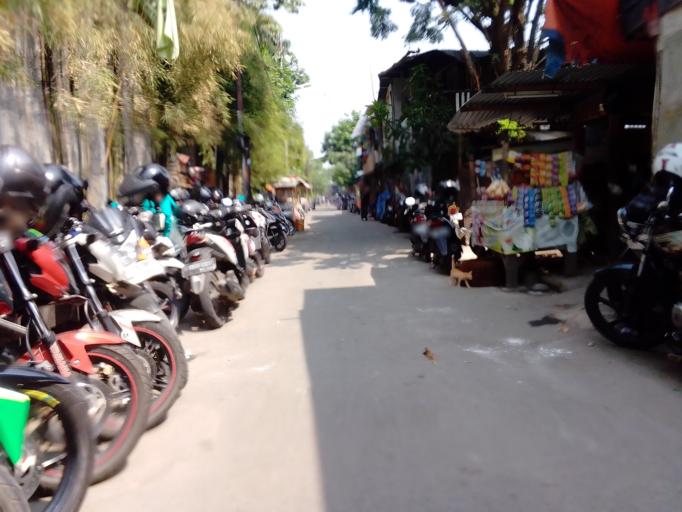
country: ID
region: Jakarta Raya
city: Jakarta
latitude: -6.2284
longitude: 106.7951
